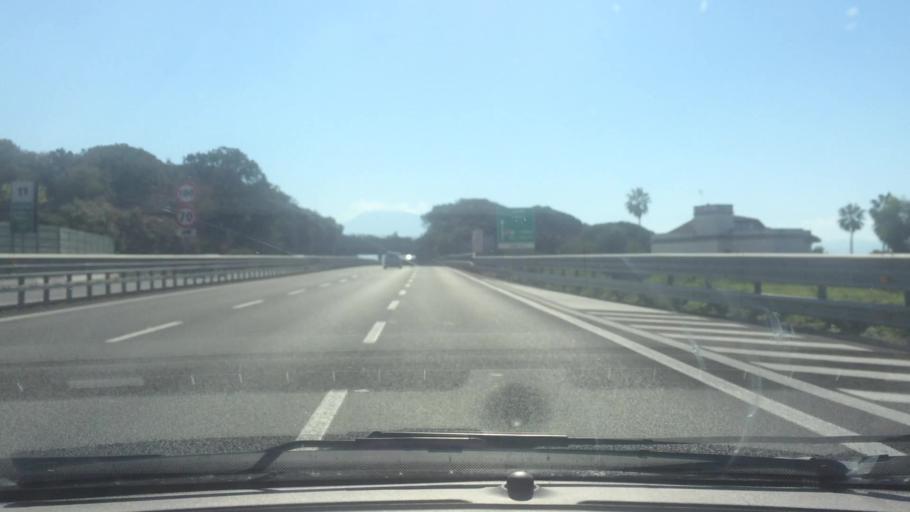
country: IT
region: Campania
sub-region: Provincia di Napoli
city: Ercolano
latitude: 40.7990
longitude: 14.3711
